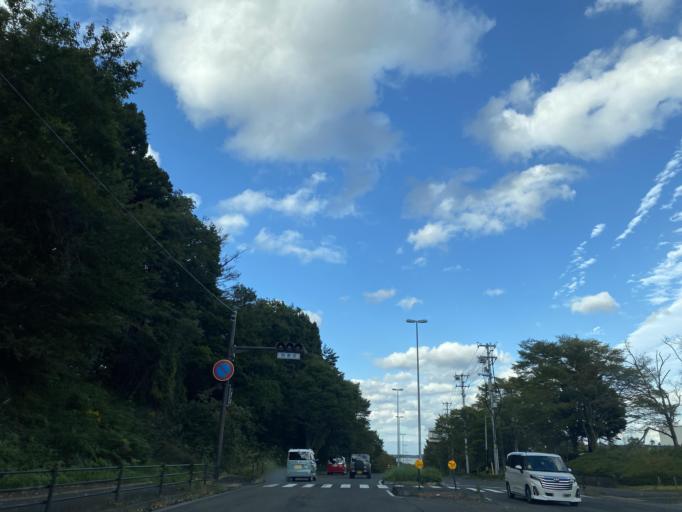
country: JP
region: Miyagi
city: Tomiya
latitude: 38.3552
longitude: 140.8436
